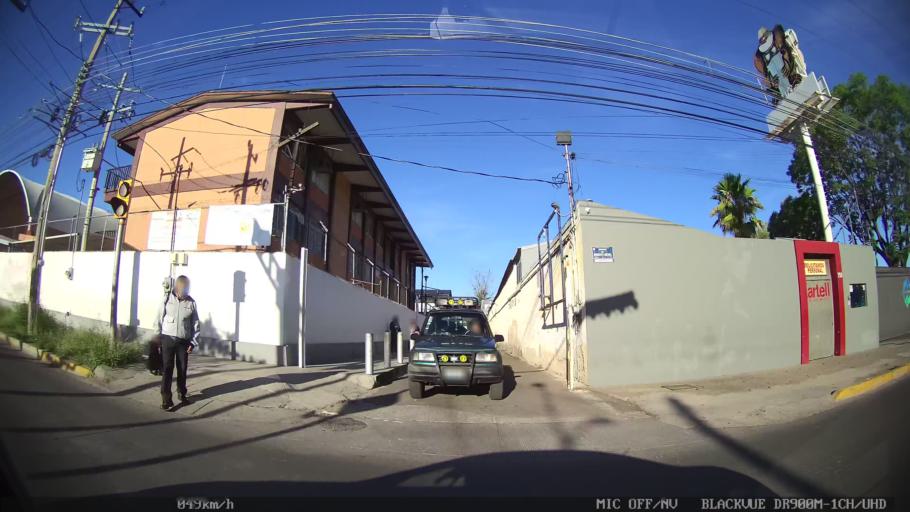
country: MX
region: Jalisco
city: Guadalajara
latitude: 20.6540
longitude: -103.3442
